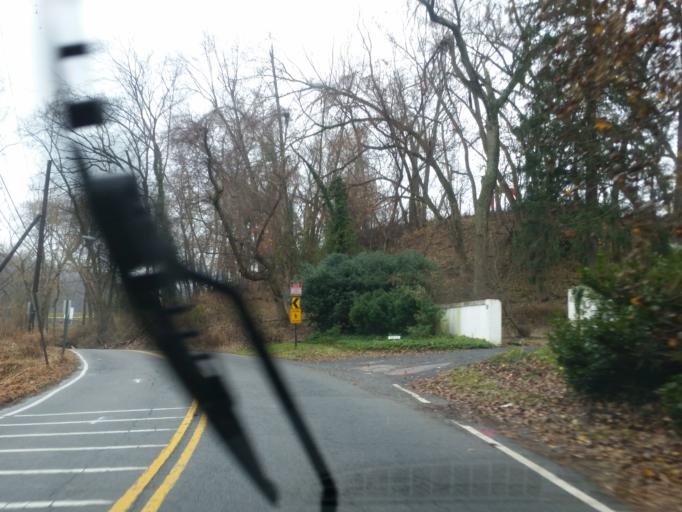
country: US
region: Maryland
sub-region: Montgomery County
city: Chevy Chase
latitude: 38.9654
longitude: -77.0545
